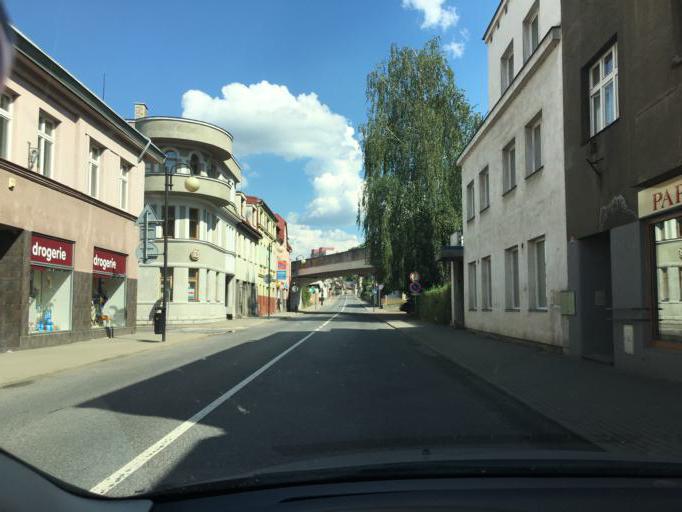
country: CZ
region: Liberecky
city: Zelezny Brod
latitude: 50.6407
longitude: 15.2570
